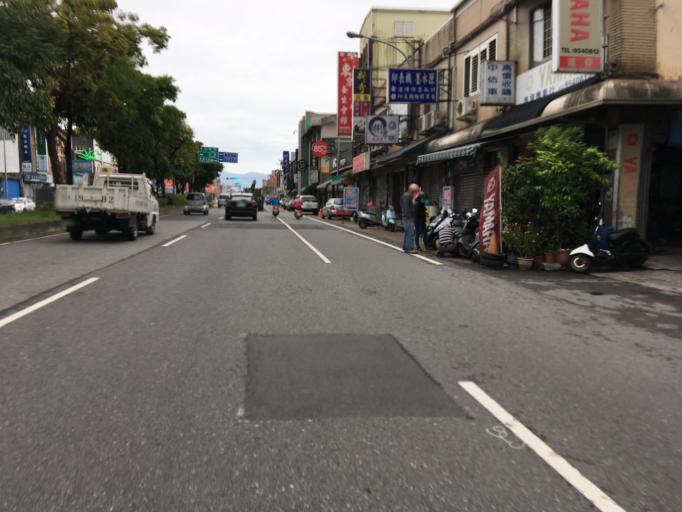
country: TW
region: Taiwan
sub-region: Yilan
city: Yilan
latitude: 24.6915
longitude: 121.7701
